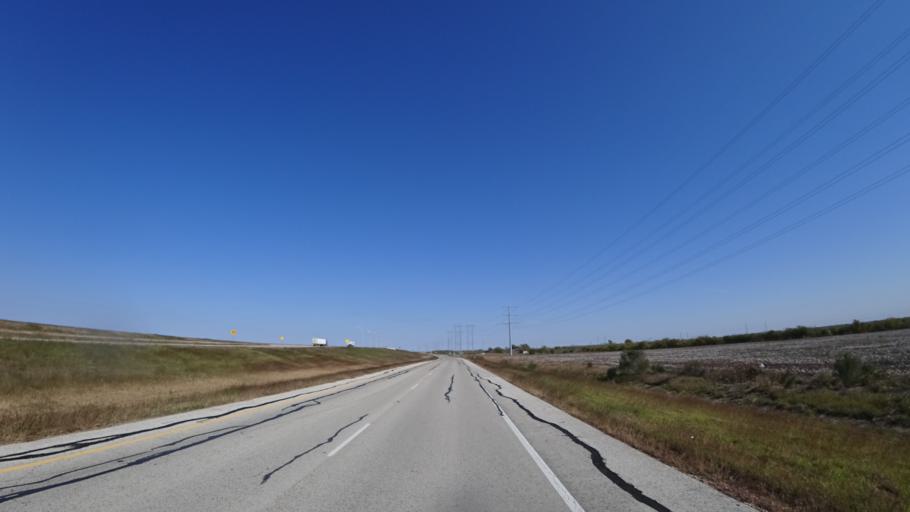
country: US
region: Texas
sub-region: Travis County
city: Onion Creek
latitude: 30.0889
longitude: -97.6815
